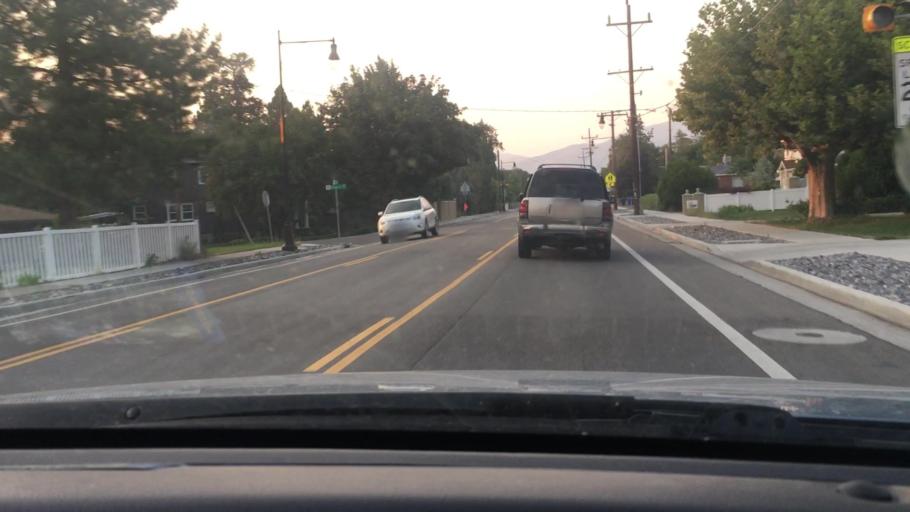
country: US
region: Utah
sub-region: Salt Lake County
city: Canyon Rim
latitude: 40.7051
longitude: -111.8244
